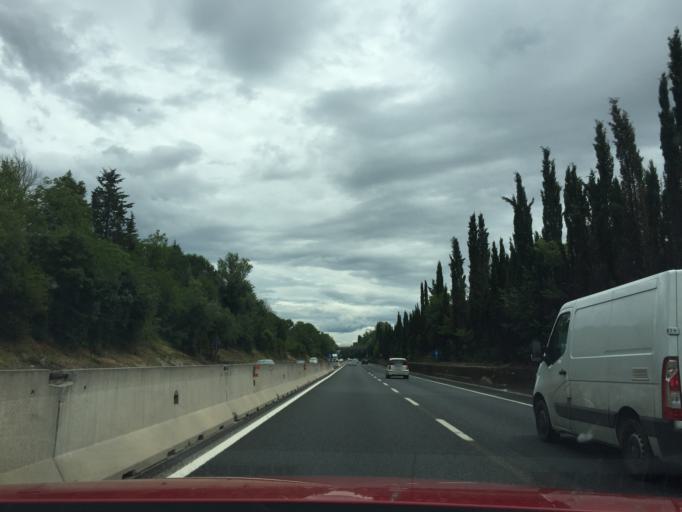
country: IT
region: Tuscany
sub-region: Province of Florence
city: Quattro Strade
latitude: 43.7383
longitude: 11.1107
